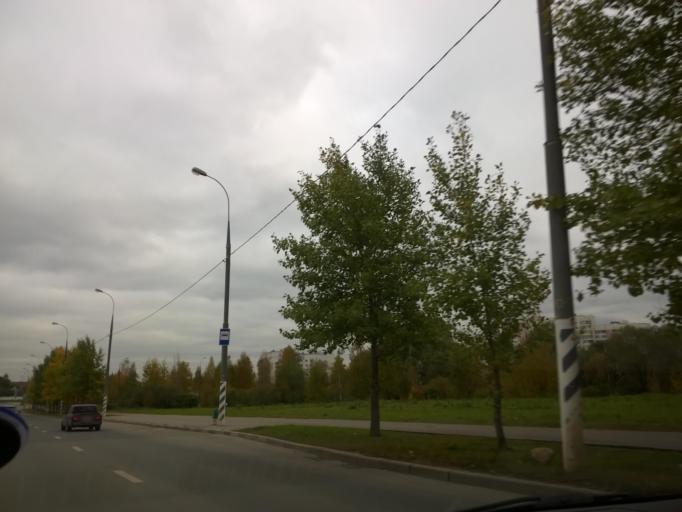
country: RU
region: Moskovskaya
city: Kommunarka
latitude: 55.5376
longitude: 37.4994
